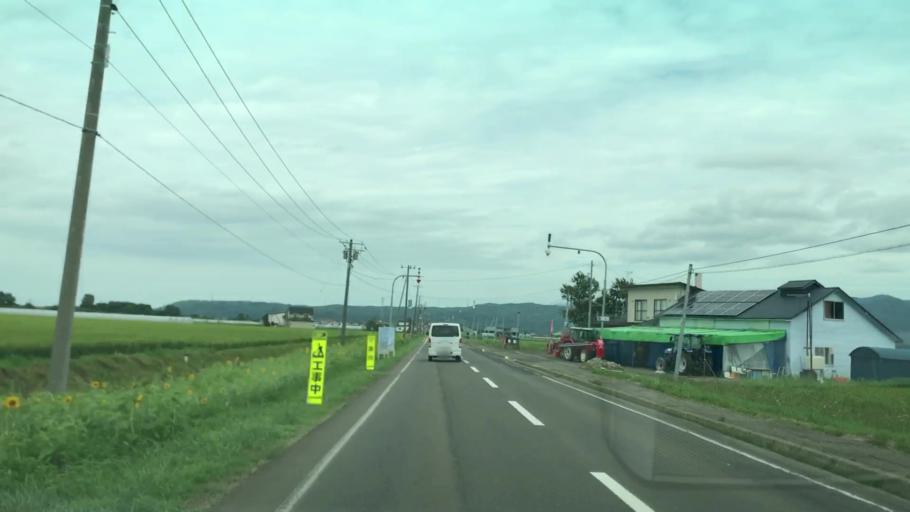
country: JP
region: Hokkaido
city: Iwanai
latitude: 43.0069
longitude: 140.5808
